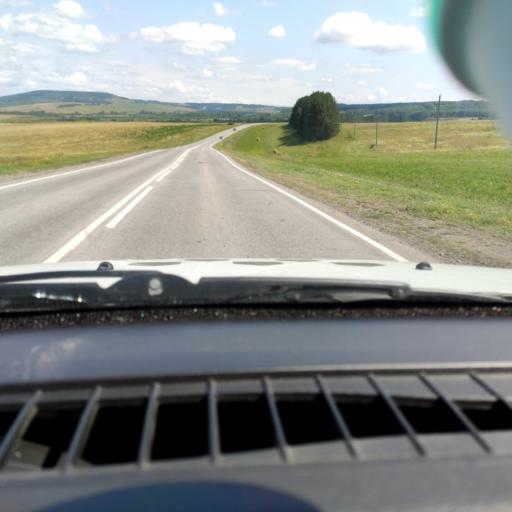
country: RU
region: Bashkortostan
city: Verkhniye Kigi
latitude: 55.3969
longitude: 58.6317
